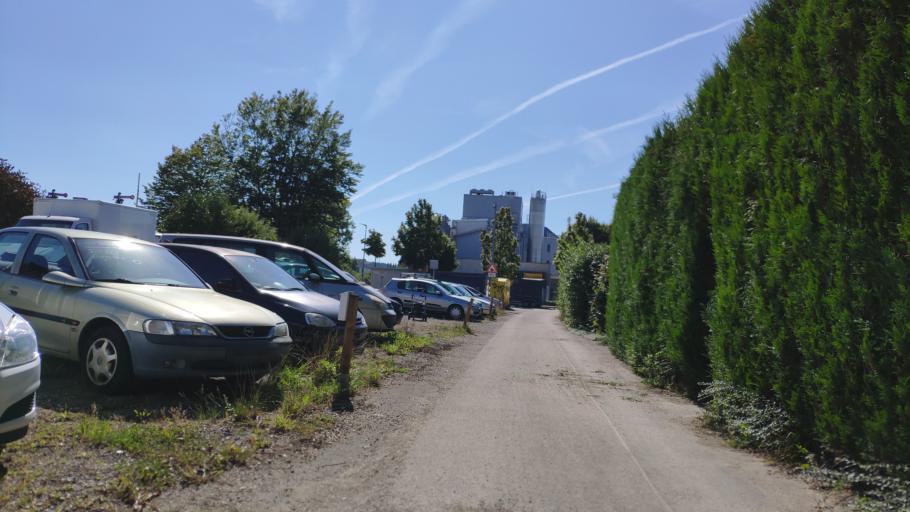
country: DE
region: Bavaria
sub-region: Swabia
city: Senden
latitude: 48.3516
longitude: 10.0365
